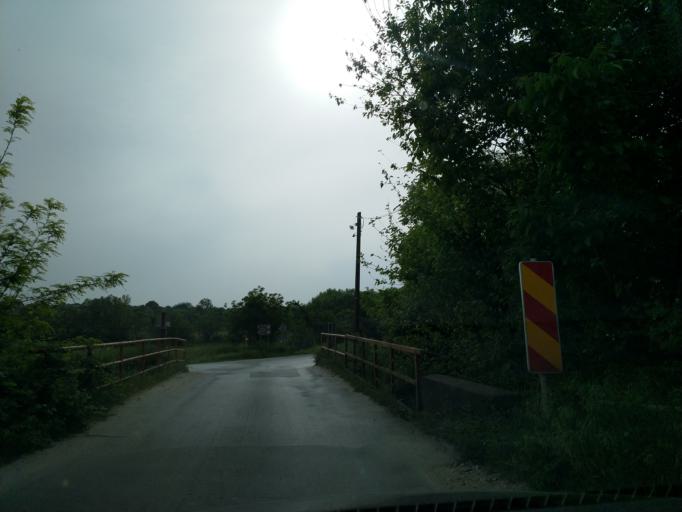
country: RS
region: Central Serbia
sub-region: Pomoravski Okrug
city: Jagodina
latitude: 43.9715
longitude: 21.2201
